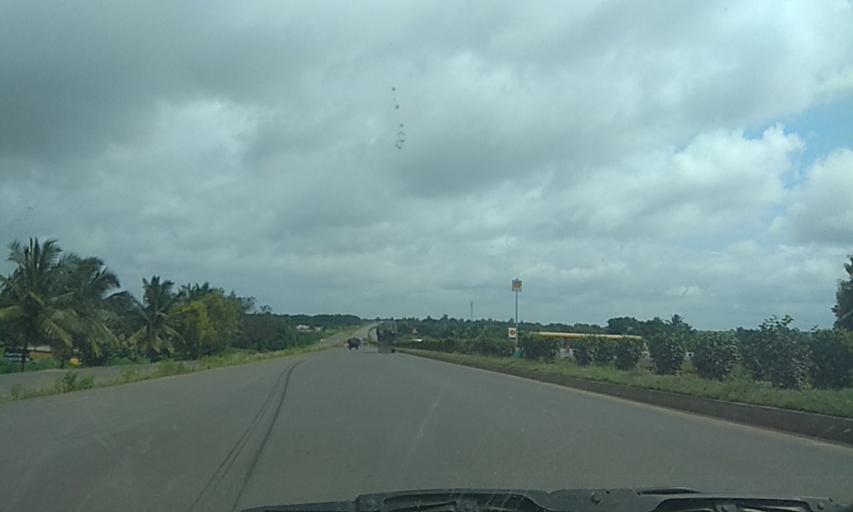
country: IN
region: Karnataka
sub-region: Dharwad
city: Kundgol
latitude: 15.2390
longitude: 75.1424
